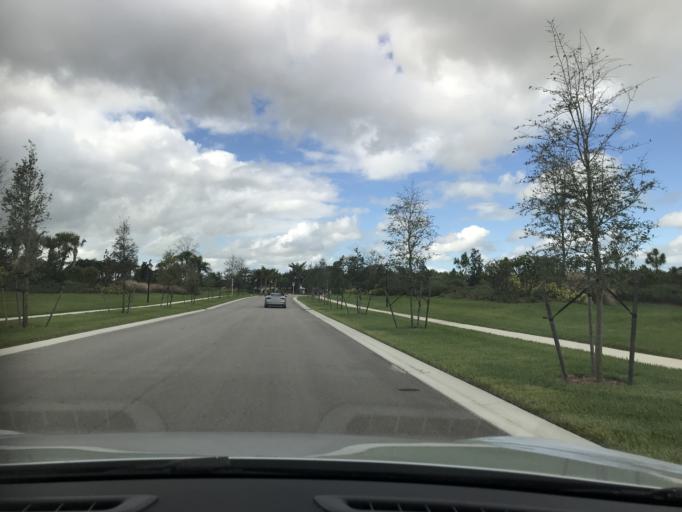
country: US
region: Florida
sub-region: Indian River County
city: Gifford
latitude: 27.6845
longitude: -80.4373
